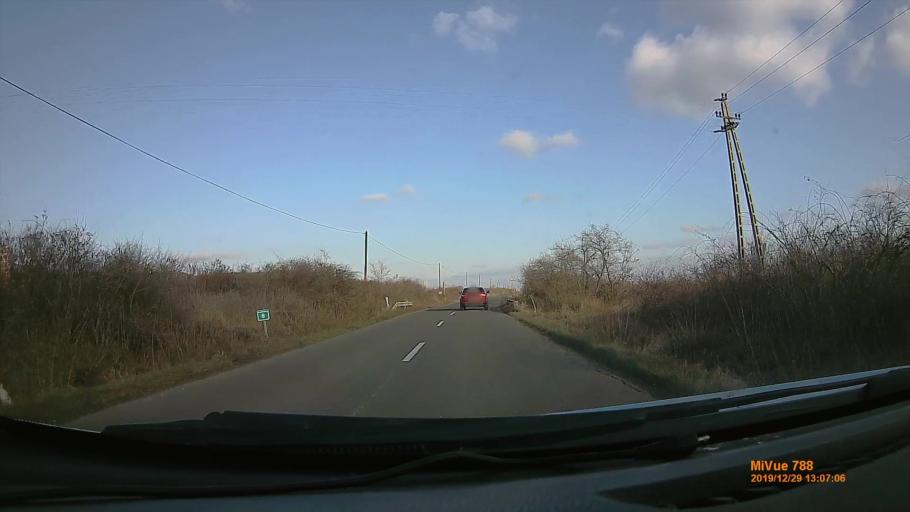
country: HU
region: Heves
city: Abasar
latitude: 47.8100
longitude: 20.0383
